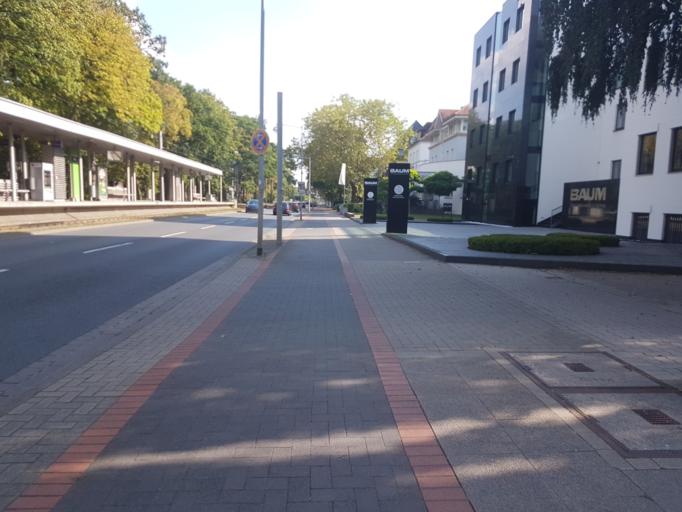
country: DE
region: Lower Saxony
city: Hannover
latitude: 52.3813
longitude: 9.7665
